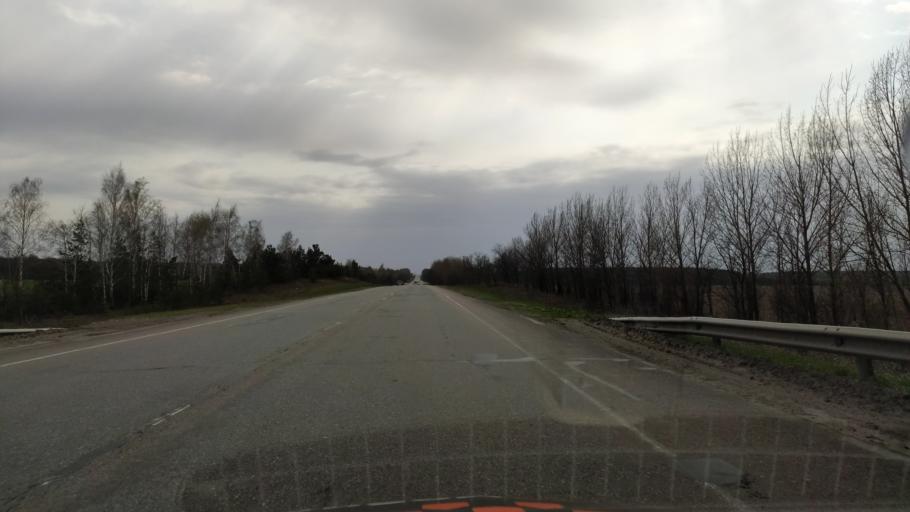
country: RU
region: Kursk
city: Gorshechnoye
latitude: 51.4433
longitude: 37.9098
